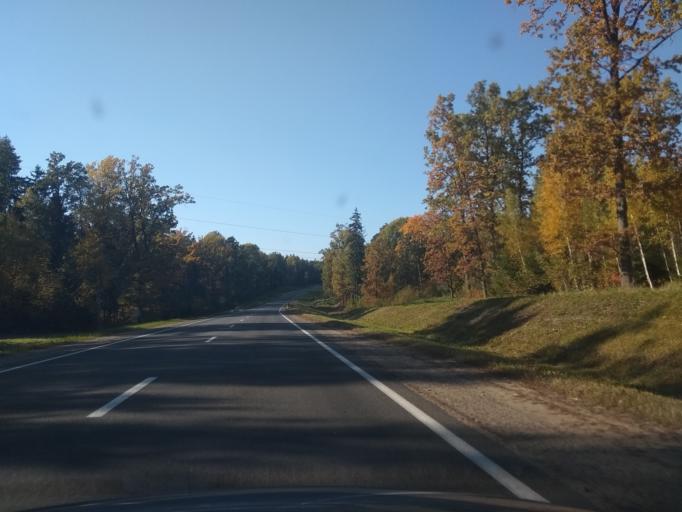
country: BY
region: Grodnenskaya
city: Slonim
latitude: 53.0589
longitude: 25.2959
